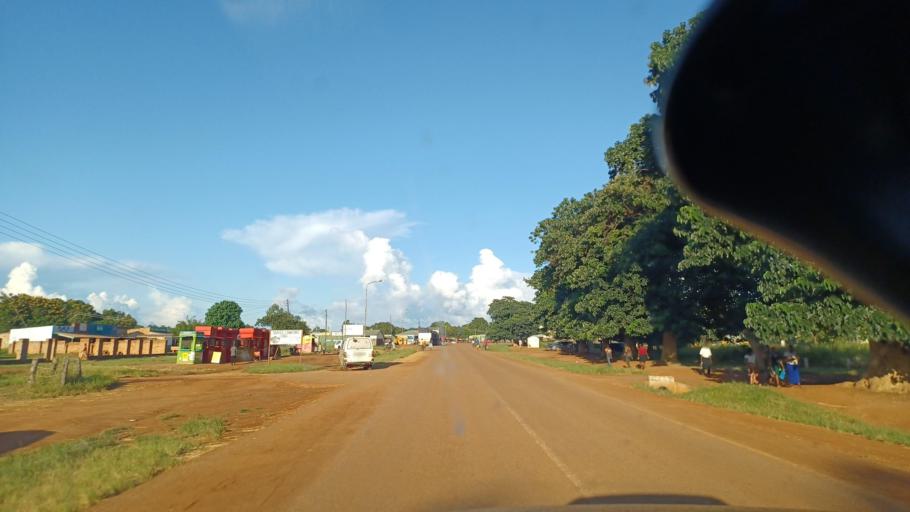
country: ZM
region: North-Western
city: Kalengwa
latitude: -13.1371
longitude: 25.0049
